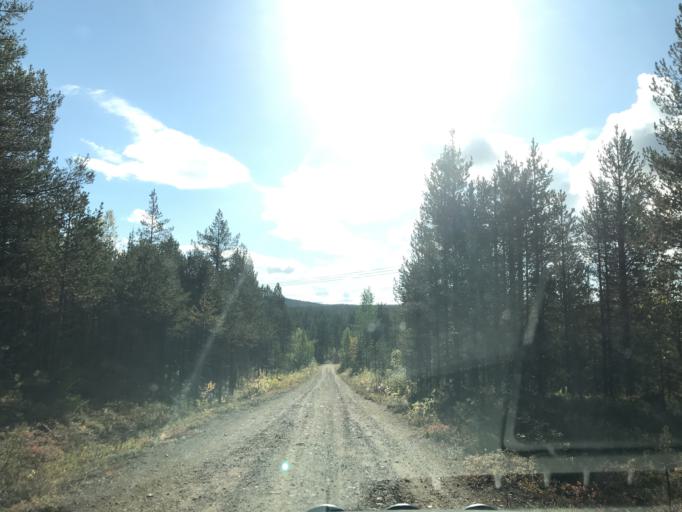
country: SE
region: Norrbotten
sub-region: Gallivare Kommun
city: Malmberget
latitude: 67.6484
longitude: 21.0834
